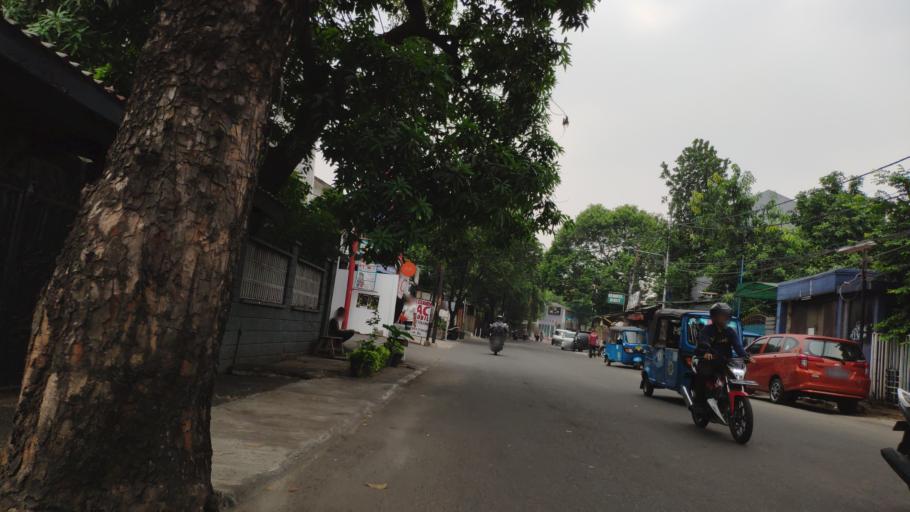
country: ID
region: Jakarta Raya
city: Jakarta
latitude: -6.2511
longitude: 106.7943
